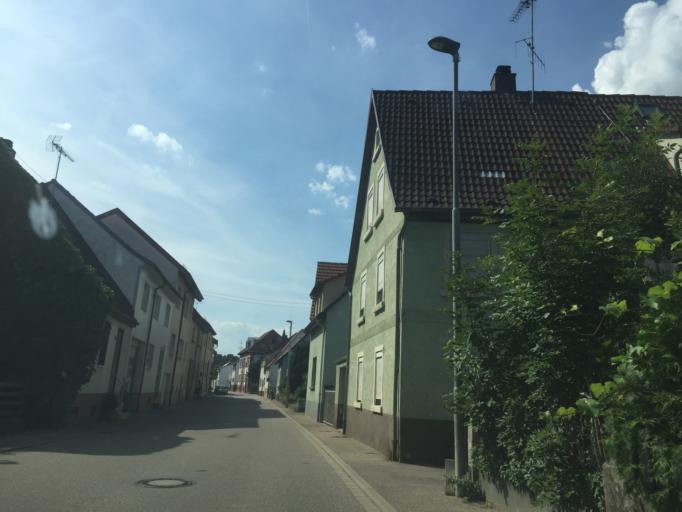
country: DE
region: Baden-Wuerttemberg
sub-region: Karlsruhe Region
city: Dielheim
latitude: 49.2999
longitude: 8.7448
